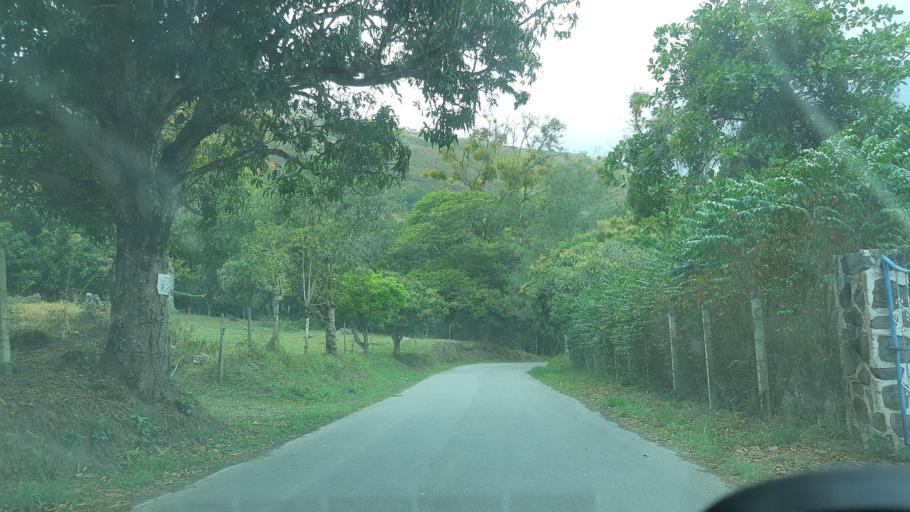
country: CO
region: Boyaca
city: Somondoco
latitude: 5.0065
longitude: -73.3669
